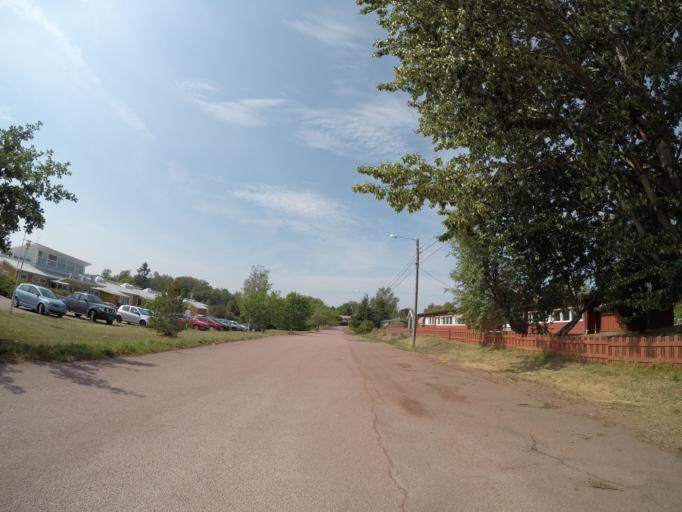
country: AX
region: Alands landsbygd
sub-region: Finstroem
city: Finstroem
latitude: 60.2322
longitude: 19.9885
